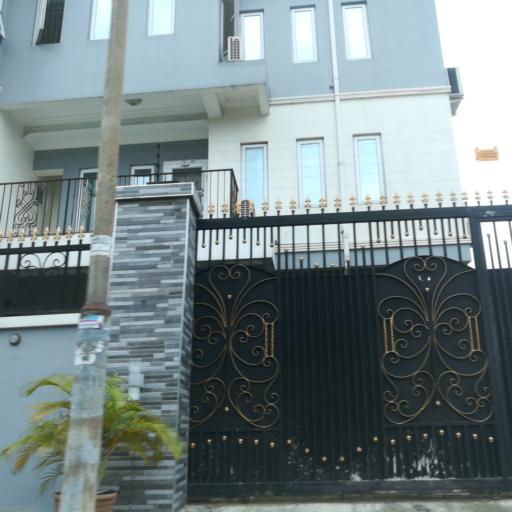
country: NG
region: Lagos
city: Makoko
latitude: 6.5026
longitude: 3.3894
